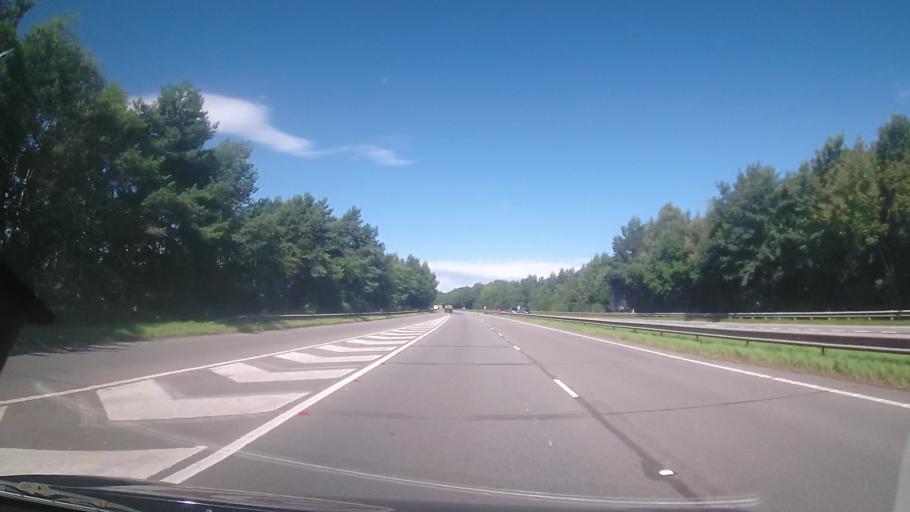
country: GB
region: Wales
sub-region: County of Flintshire
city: Hawarden
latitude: 53.1626
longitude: -3.0129
